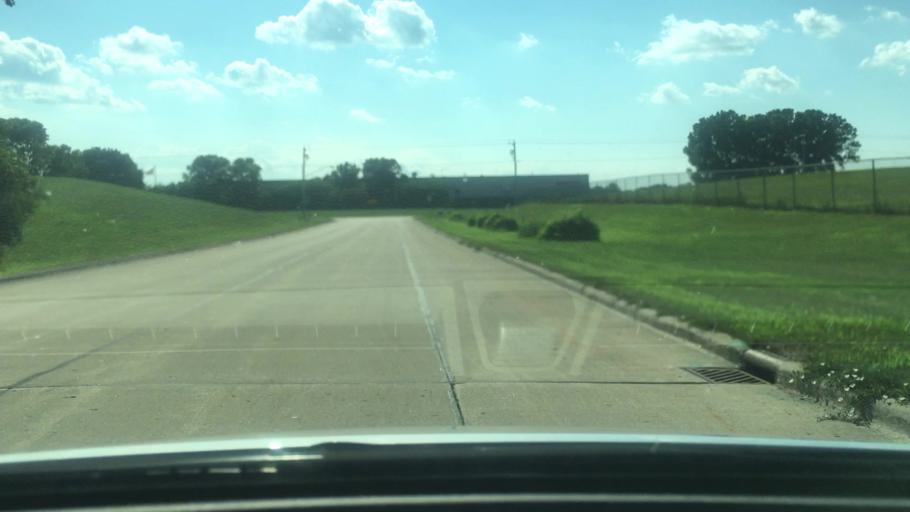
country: US
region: Wisconsin
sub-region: Winnebago County
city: Oshkosh
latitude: 43.9735
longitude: -88.5482
